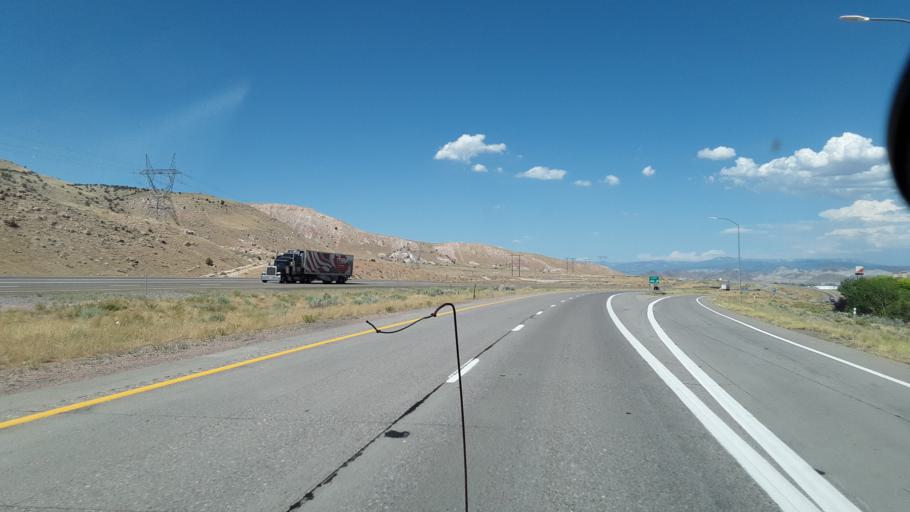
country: US
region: Utah
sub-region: Sevier County
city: Richfield
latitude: 38.7857
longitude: -112.0885
